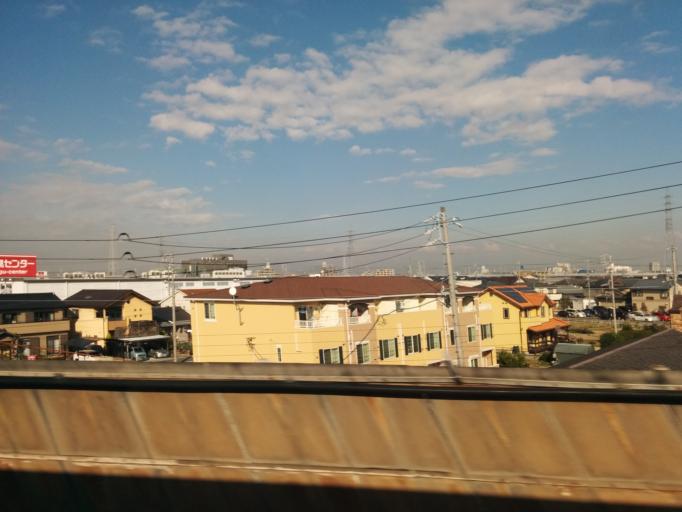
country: JP
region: Aichi
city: Chiryu
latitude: 34.9995
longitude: 137.0241
